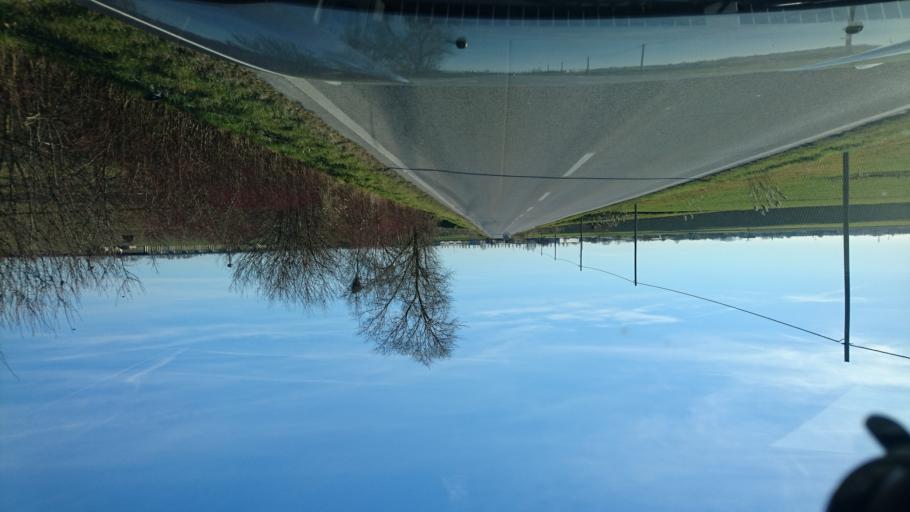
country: IT
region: Veneto
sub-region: Provincia di Rovigo
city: Corbola
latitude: 45.0101
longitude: 12.1092
